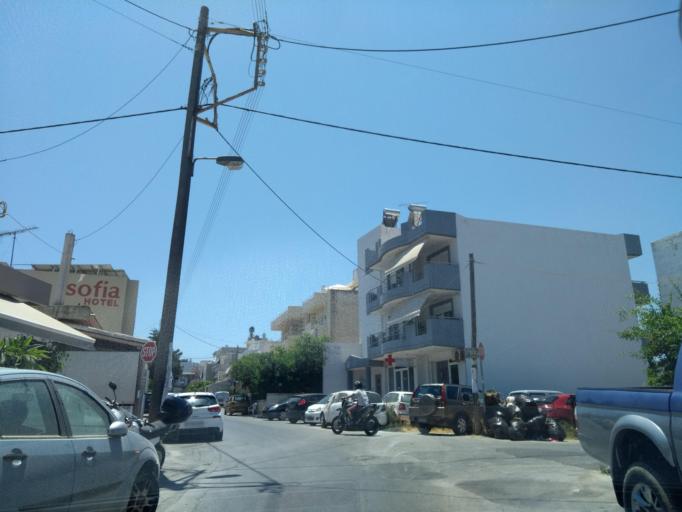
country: GR
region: Crete
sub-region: Nomos Irakleiou
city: Nea Alikarnassos
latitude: 35.3368
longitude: 25.1605
